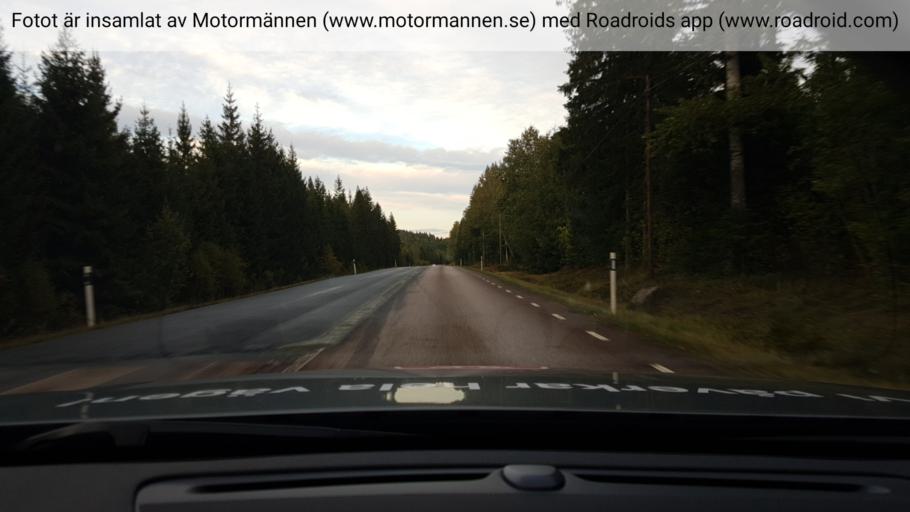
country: SE
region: Vaestra Goetaland
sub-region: Amals Kommun
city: Amal
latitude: 59.0550
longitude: 12.5003
